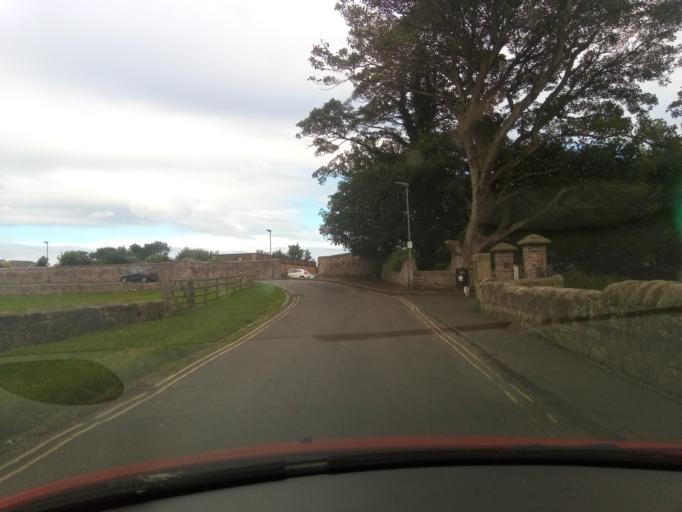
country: GB
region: England
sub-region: Northumberland
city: Berwick-Upon-Tweed
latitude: 55.7720
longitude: -1.9994
